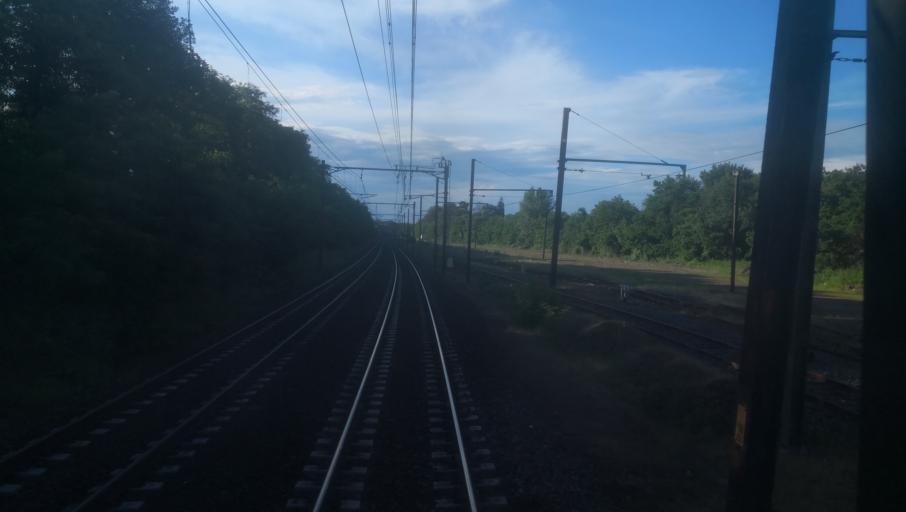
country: FR
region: Centre
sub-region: Departement du Cher
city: Vierzon
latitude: 47.2447
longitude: 2.0458
